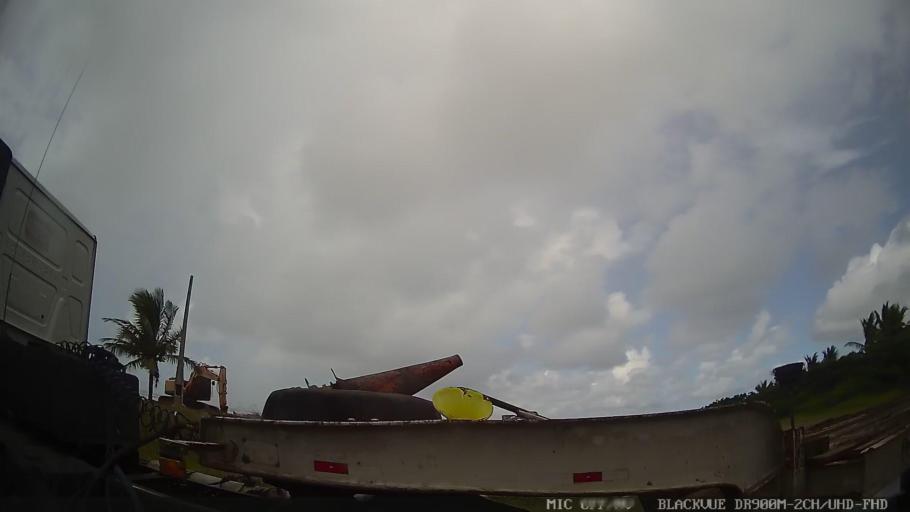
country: BR
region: Sao Paulo
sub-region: Itanhaem
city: Itanhaem
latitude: -24.2244
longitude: -46.8569
